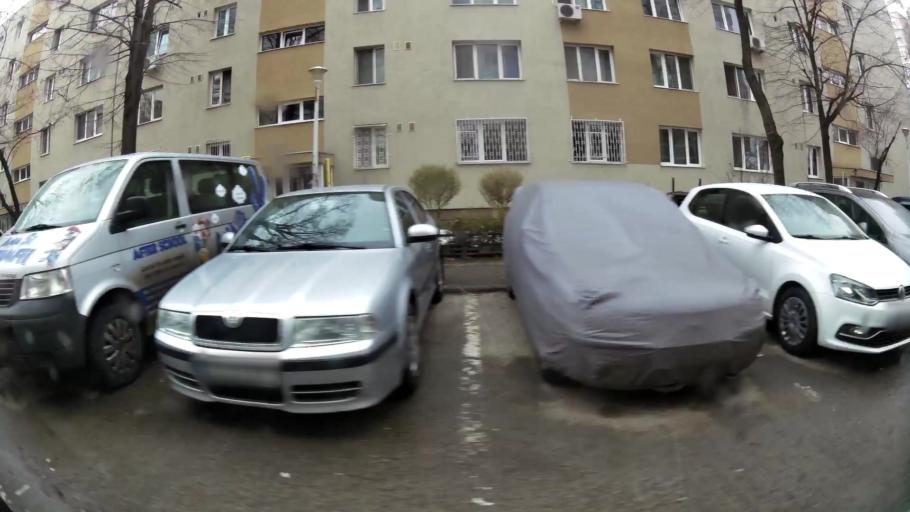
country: RO
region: Ilfov
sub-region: Comuna Chiajna
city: Rosu
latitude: 44.4166
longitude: 26.0304
